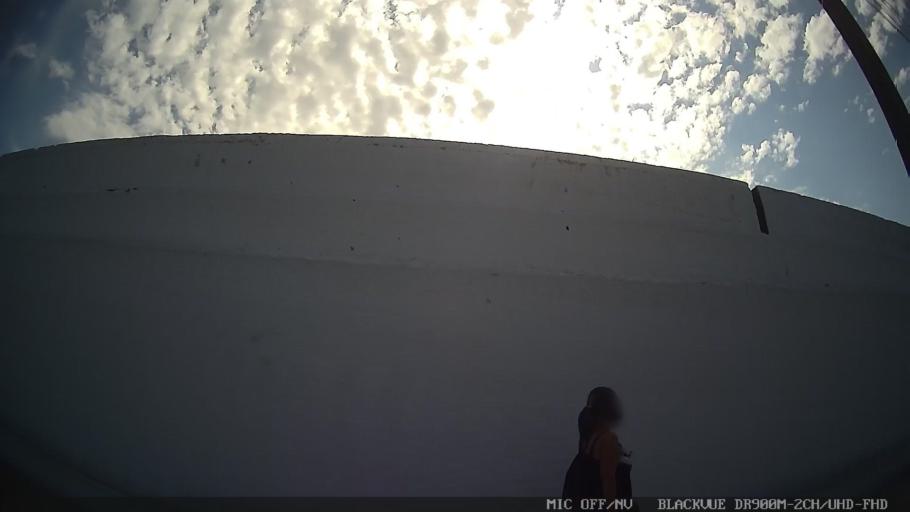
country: BR
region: Sao Paulo
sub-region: Santos
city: Santos
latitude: -23.9409
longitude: -46.2883
